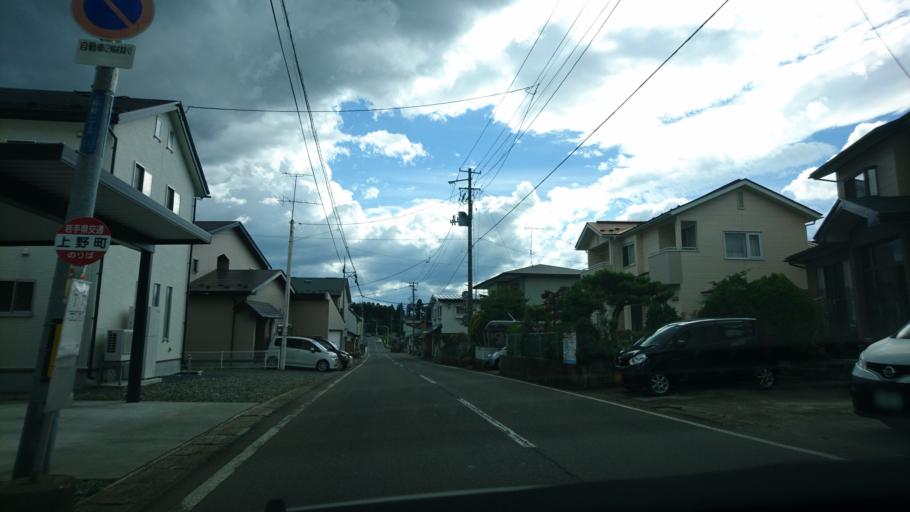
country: JP
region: Iwate
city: Kitakami
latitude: 39.2989
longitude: 141.1254
